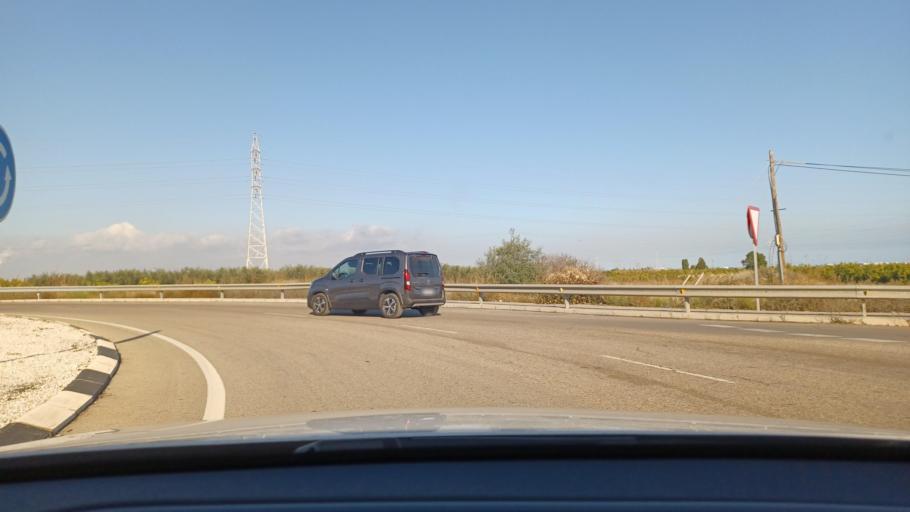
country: ES
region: Valencia
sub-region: Provincia de Castello
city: Moncofar
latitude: 39.8134
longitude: -0.1607
